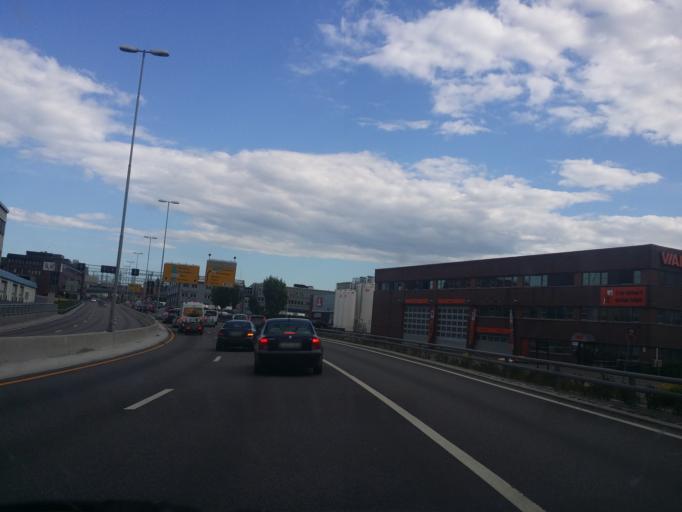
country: NO
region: Oslo
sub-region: Oslo
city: Oslo
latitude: 59.9267
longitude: 10.8025
